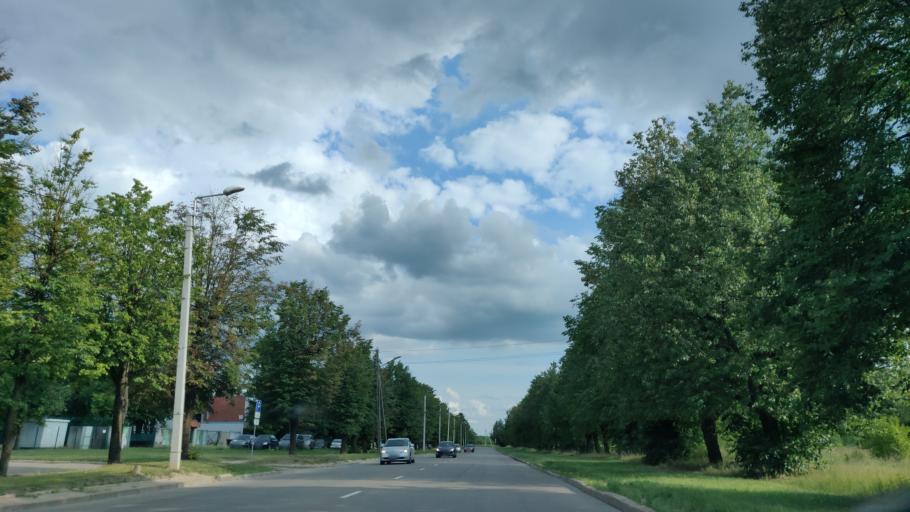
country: LT
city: Baltoji Voke
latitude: 54.6231
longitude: 25.1418
